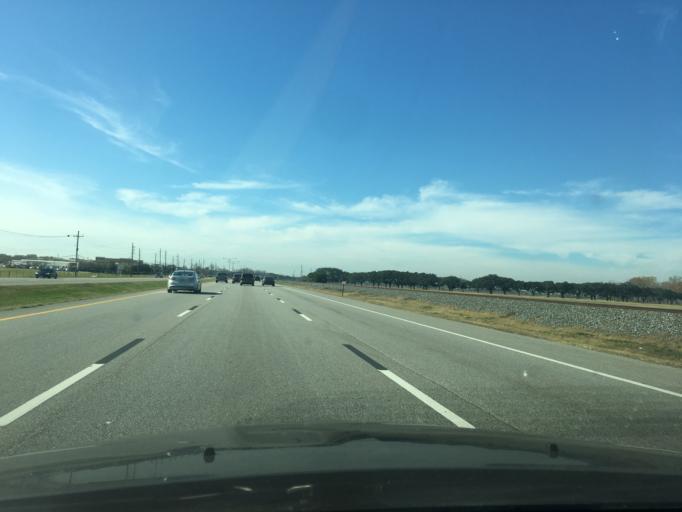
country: US
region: Texas
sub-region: Fort Bend County
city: Sugar Land
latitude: 29.6111
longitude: -95.6547
